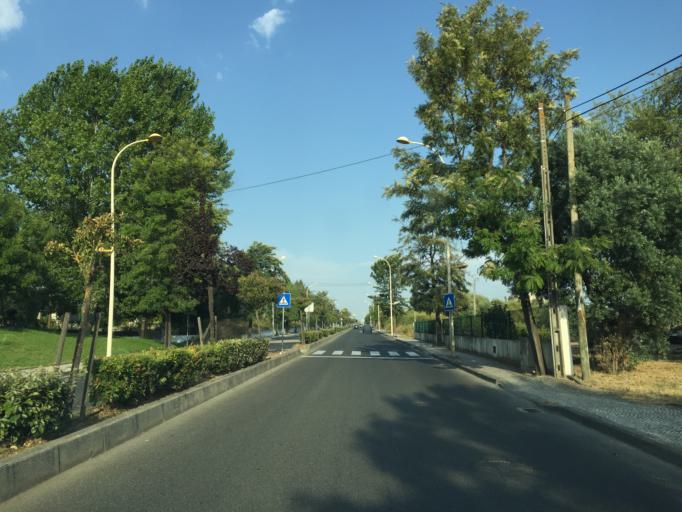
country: PT
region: Santarem
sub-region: Torres Novas
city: Torres Novas
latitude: 39.4718
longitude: -8.5442
